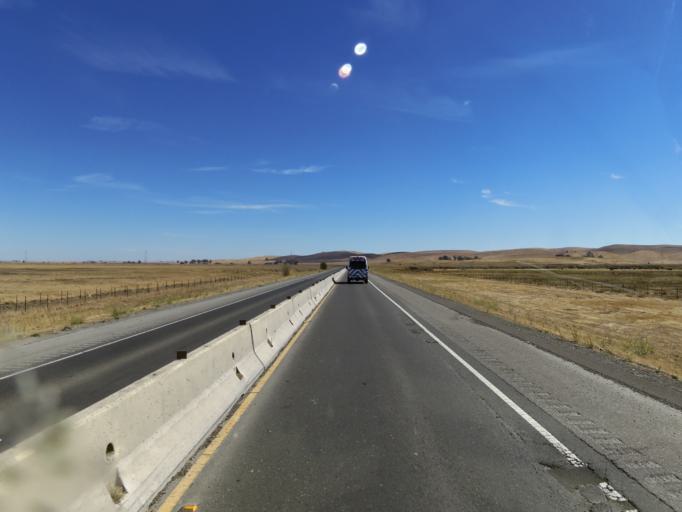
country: US
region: California
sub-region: Solano County
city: Suisun
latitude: 38.2337
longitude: -121.9816
